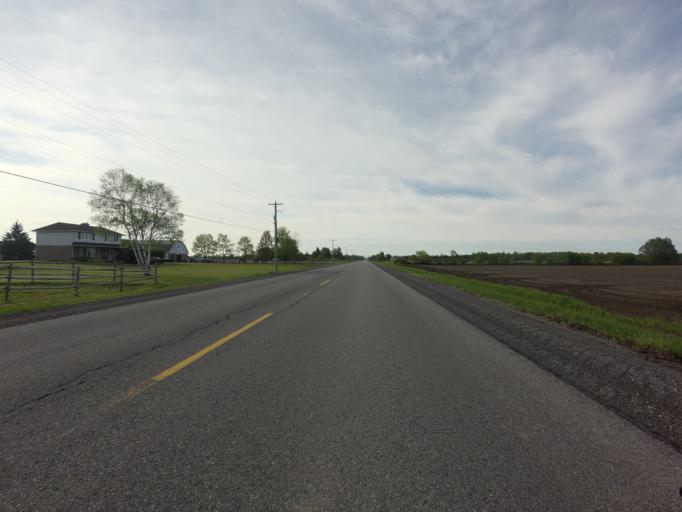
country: CA
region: Ontario
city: Ottawa
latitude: 45.2999
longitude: -75.4535
